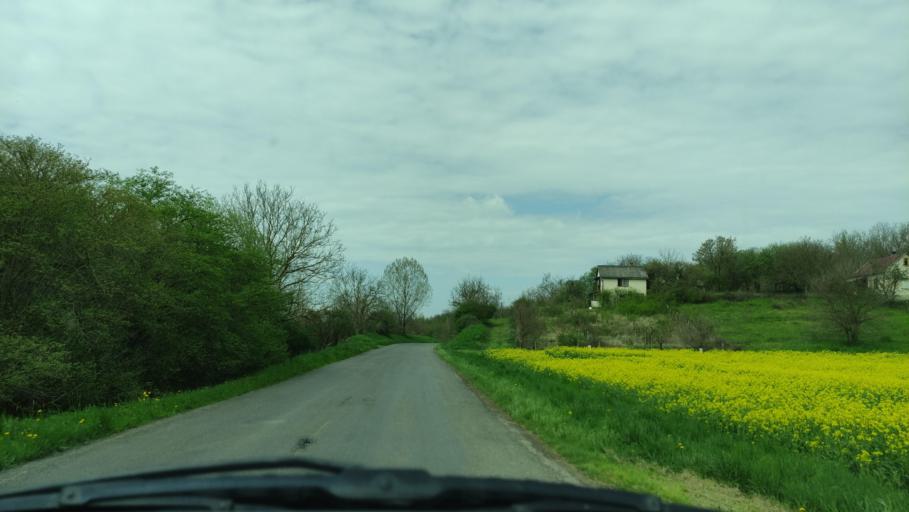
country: HU
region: Baranya
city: Sasd
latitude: 46.3061
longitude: 18.1595
